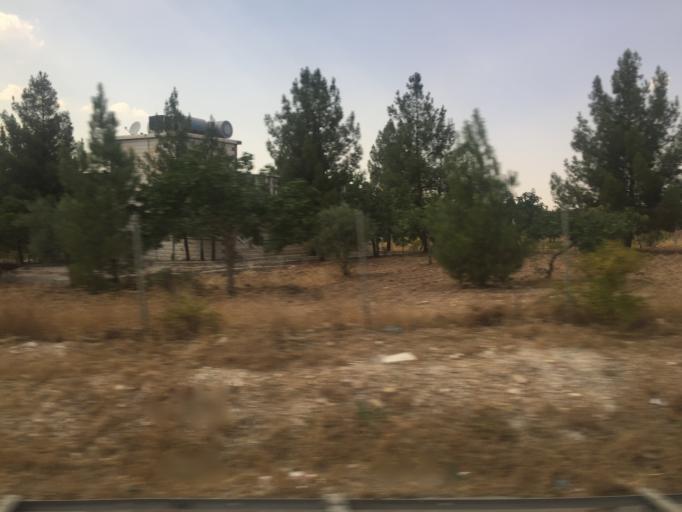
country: TR
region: Sanliurfa
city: Akziyaret
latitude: 37.2700
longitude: 38.7984
